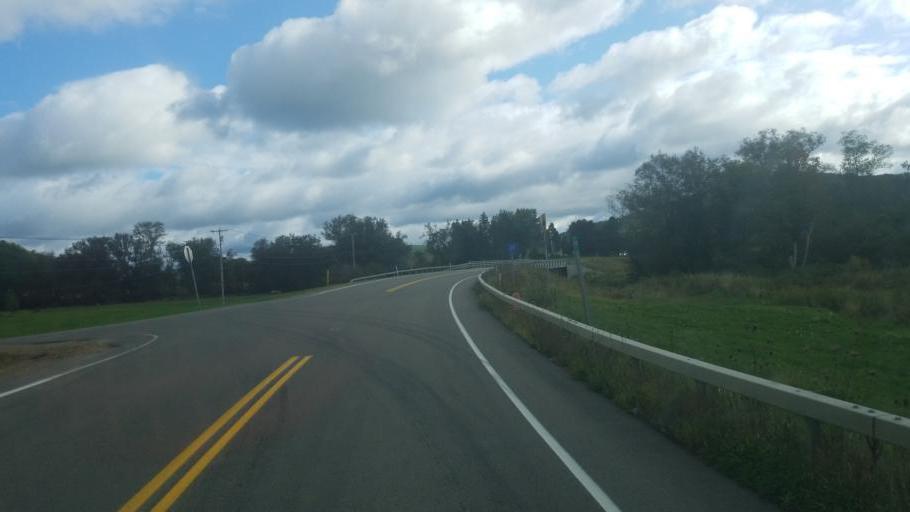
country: US
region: New York
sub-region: Cattaraugus County
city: Weston Mills
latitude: 42.0879
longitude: -78.3657
